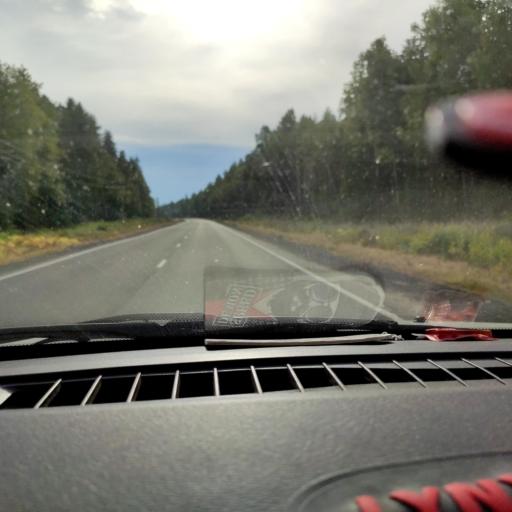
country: RU
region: Perm
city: Polazna
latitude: 58.1954
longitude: 56.2664
